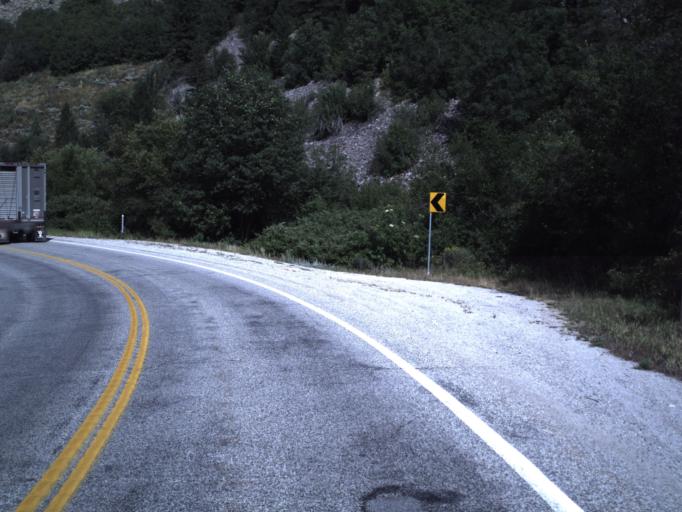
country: US
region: Utah
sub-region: Cache County
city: North Logan
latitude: 41.8195
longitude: -111.6136
